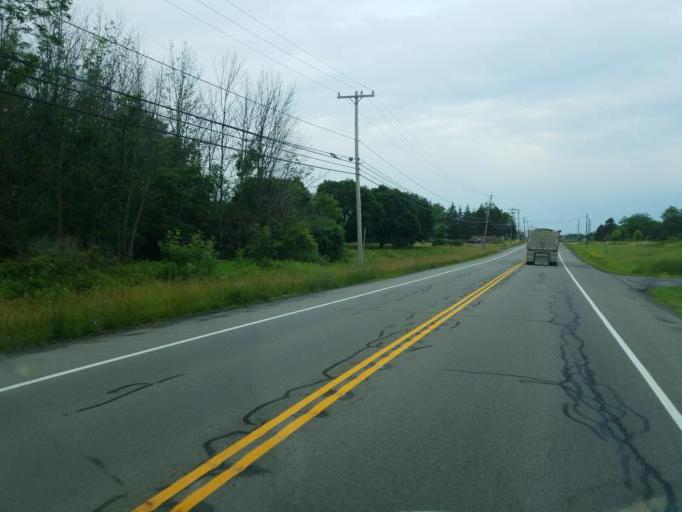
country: US
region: New York
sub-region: Niagara County
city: Lewiston
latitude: 43.1300
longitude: -79.0104
